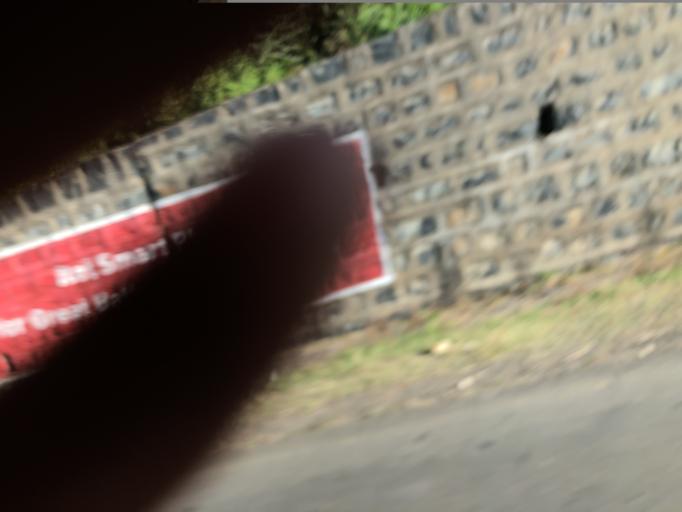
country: ET
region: Amhara
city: Debre Tabor
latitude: 11.9256
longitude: 37.9471
